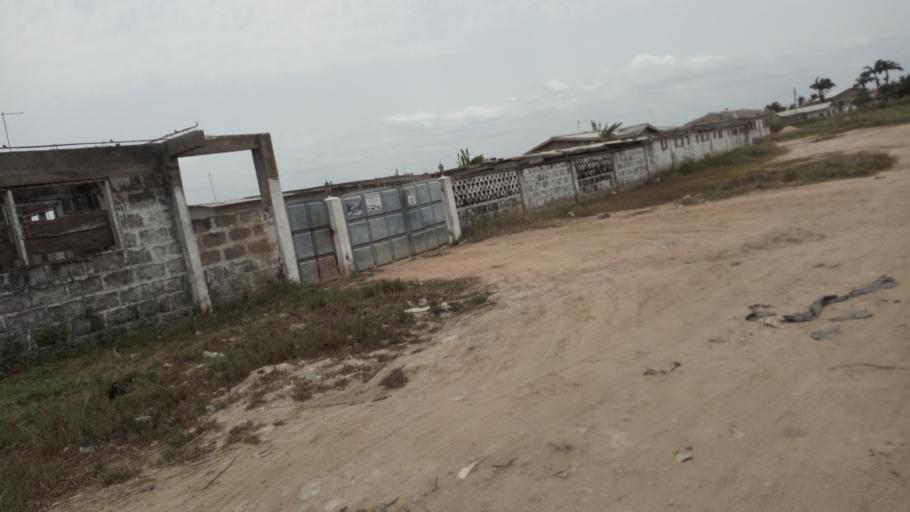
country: GH
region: Central
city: Winneba
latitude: 5.3474
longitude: -0.6342
